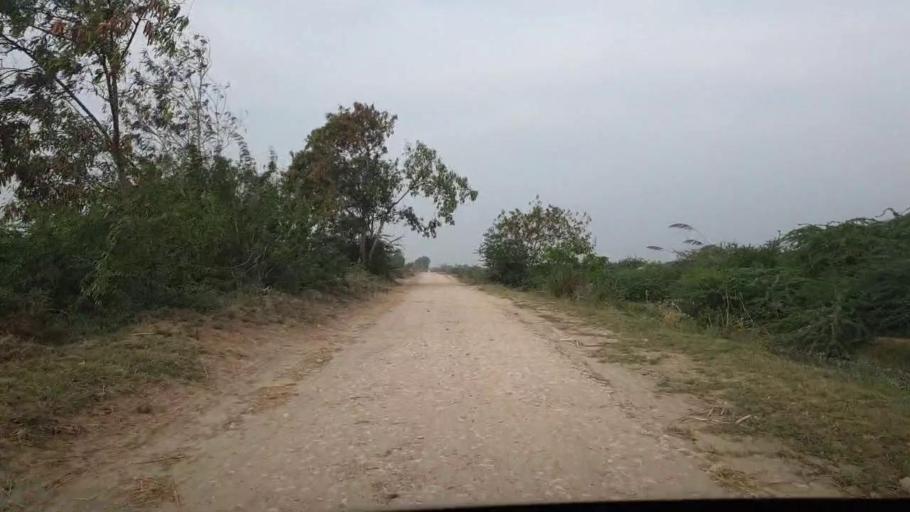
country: PK
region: Sindh
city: Chuhar Jamali
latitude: 24.4122
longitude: 67.9446
